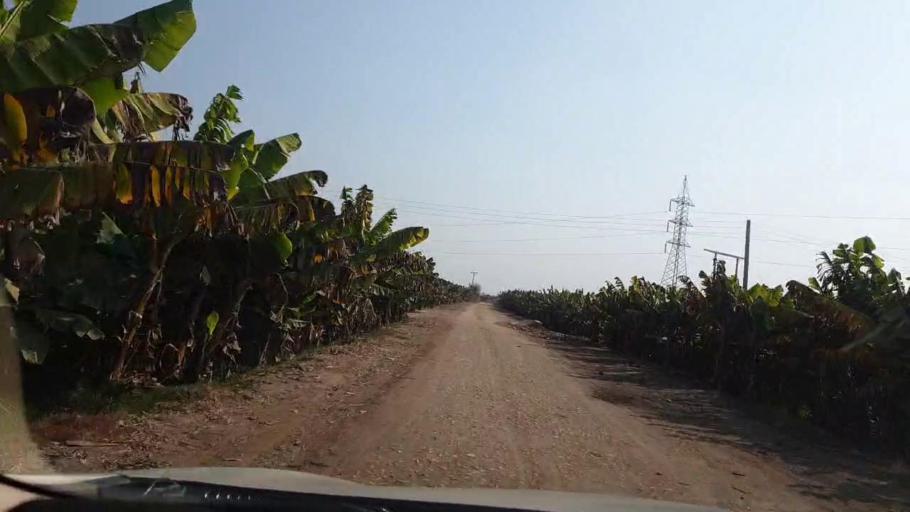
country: PK
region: Sindh
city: Matiari
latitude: 25.6265
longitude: 68.4937
